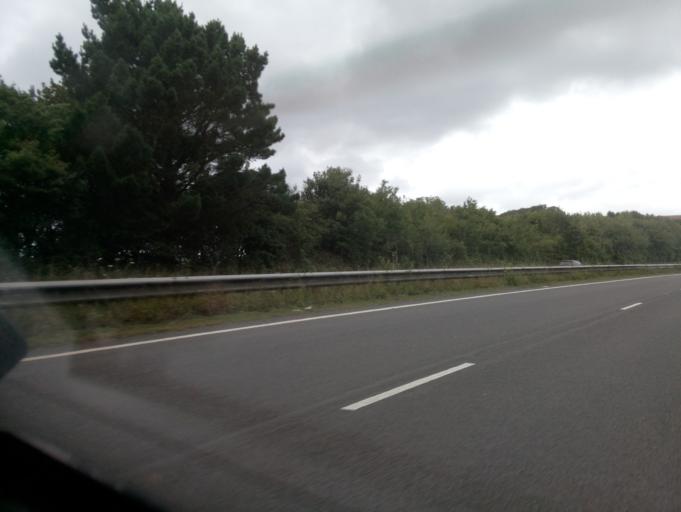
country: GB
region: England
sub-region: Devon
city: Marldon
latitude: 50.4612
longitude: -3.5899
